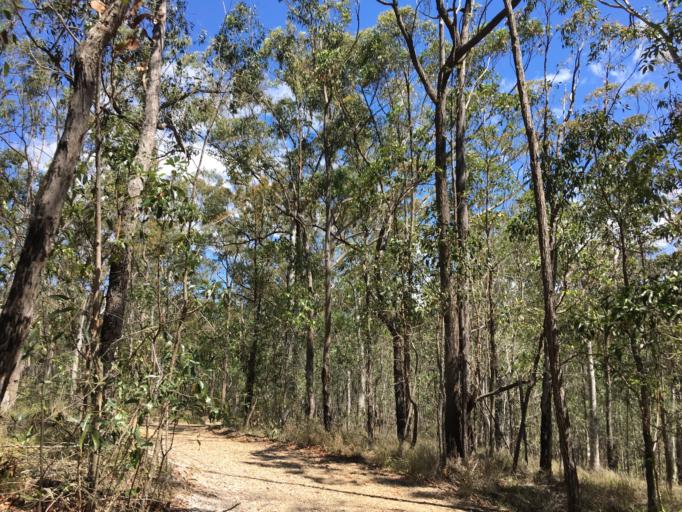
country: AU
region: Queensland
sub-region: Logan
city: Woodridge
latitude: -27.6263
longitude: 153.0895
